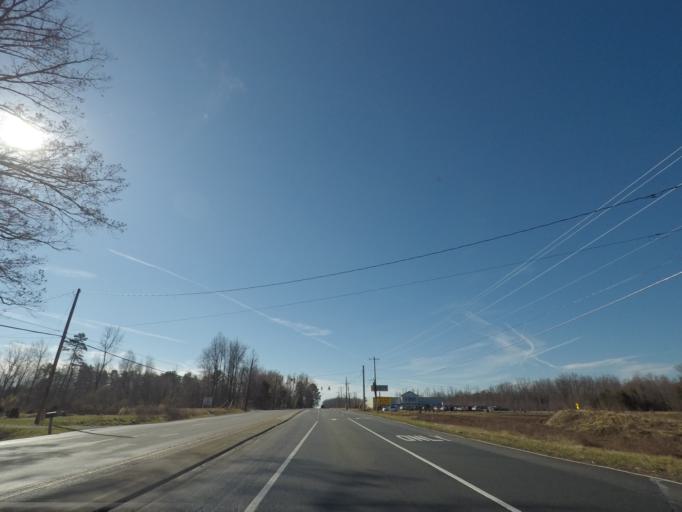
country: US
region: North Carolina
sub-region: Guilford County
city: Pleasant Garden
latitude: 35.9979
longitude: -79.7926
